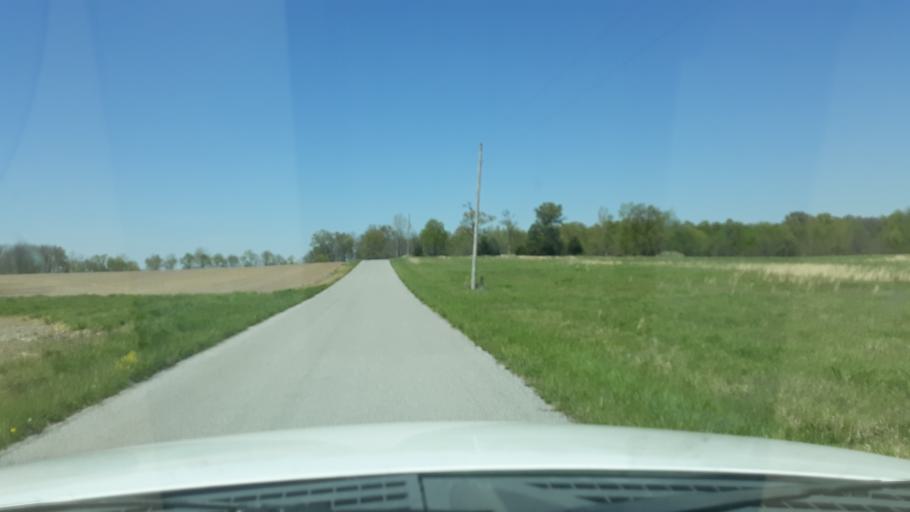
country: US
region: Illinois
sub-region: Saline County
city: Harrisburg
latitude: 37.8901
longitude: -88.6698
